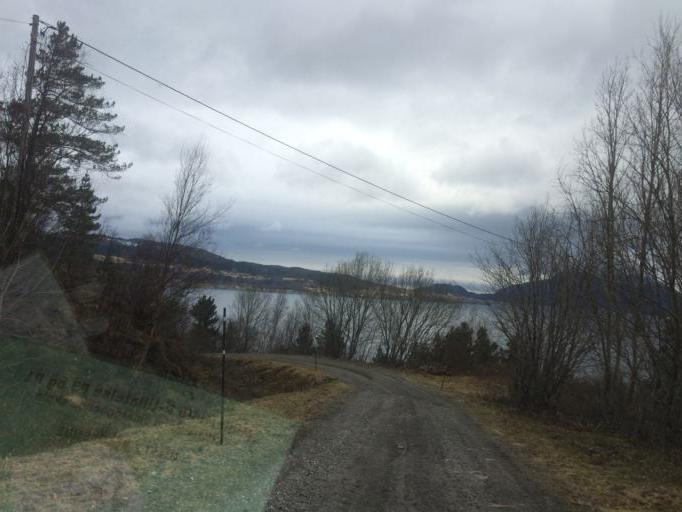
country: NO
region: More og Romsdal
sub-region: Gjemnes
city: Batnfjordsora
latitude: 62.9649
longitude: 7.7329
